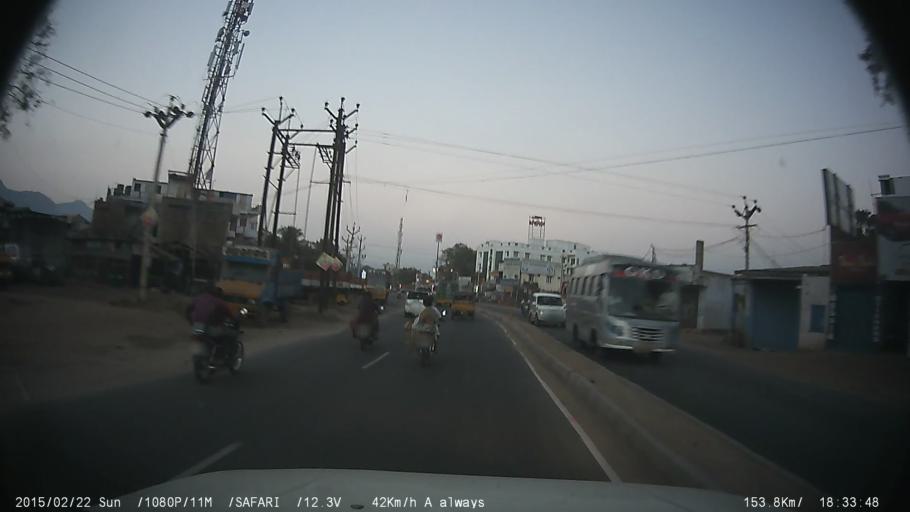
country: IN
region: Tamil Nadu
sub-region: Theni
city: Teni
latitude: 10.0053
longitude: 77.4716
